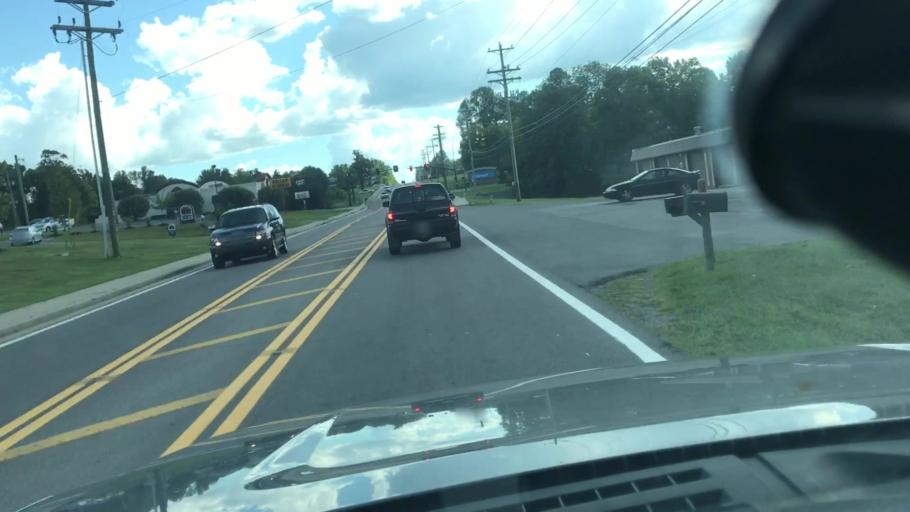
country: US
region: Tennessee
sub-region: Williamson County
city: Fairview
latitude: 35.9633
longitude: -87.1350
